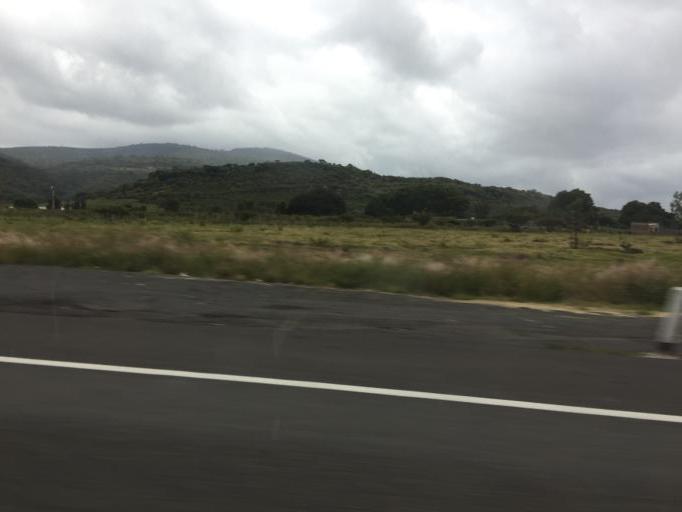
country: MX
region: Jalisco
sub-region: Zapotlanejo
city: La Mezquitera
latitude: 20.5406
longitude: -103.0235
